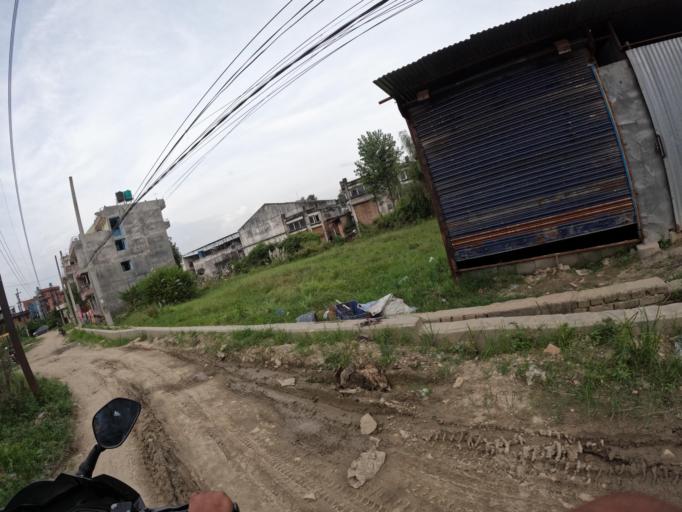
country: NP
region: Central Region
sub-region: Bagmati Zone
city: Bhaktapur
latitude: 27.6806
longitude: 85.3912
